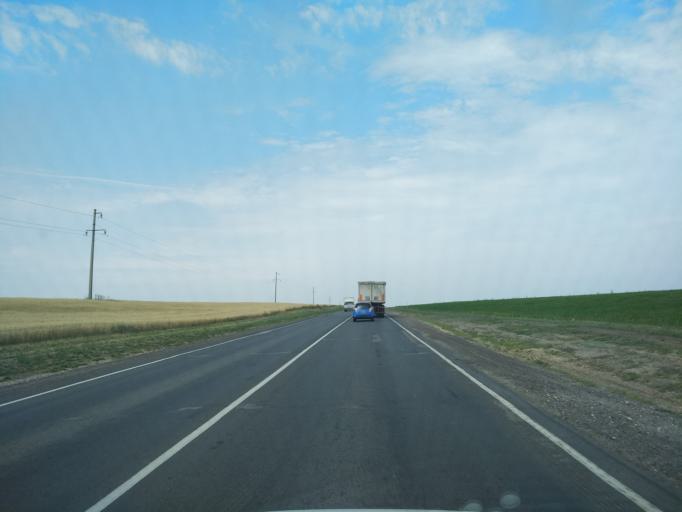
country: RU
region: Voronezj
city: Orlovo
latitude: 51.6823
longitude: 39.5680
